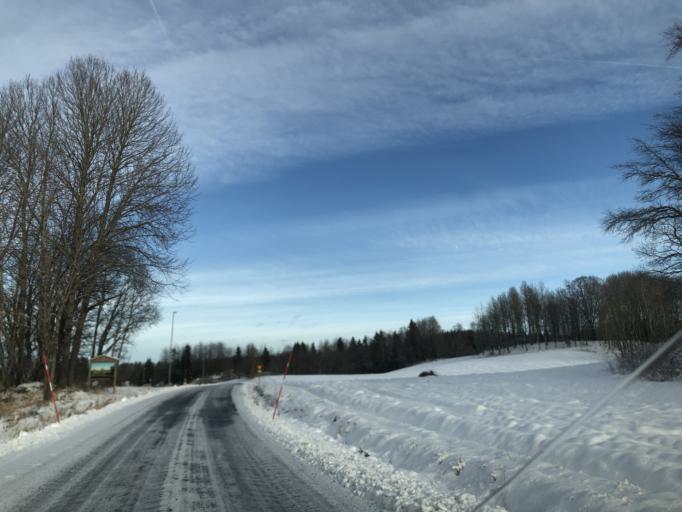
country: SE
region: Vaestra Goetaland
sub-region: Ulricehamns Kommun
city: Ulricehamn
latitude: 57.7951
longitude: 13.5357
